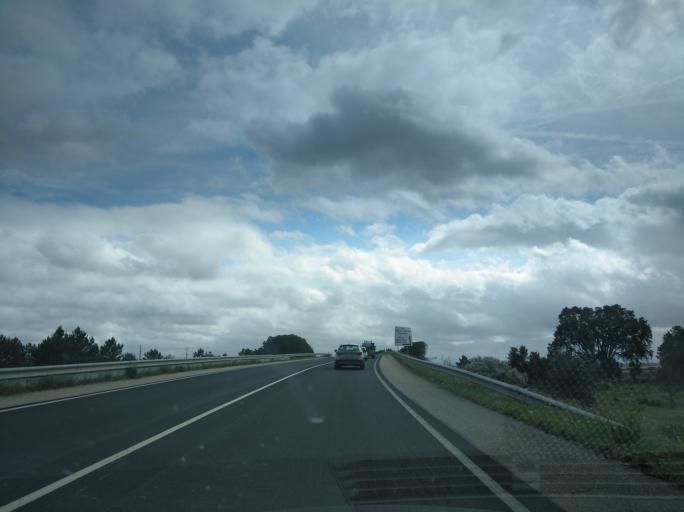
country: PT
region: Setubal
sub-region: Palmela
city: Pinhal Novo
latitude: 38.6719
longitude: -8.8961
